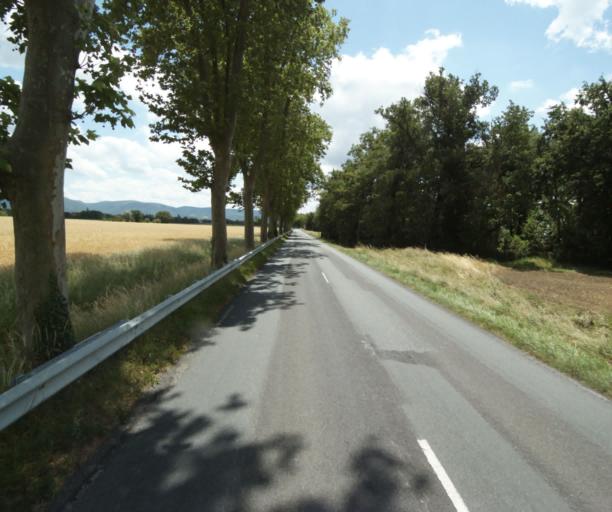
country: FR
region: Midi-Pyrenees
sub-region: Departement de la Haute-Garonne
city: Revel
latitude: 43.4992
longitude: 2.0122
